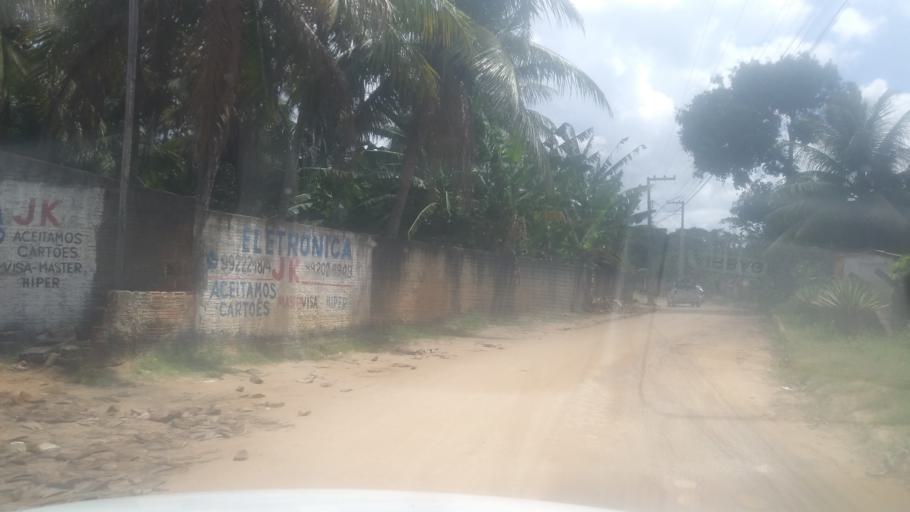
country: BR
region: Rio Grande do Norte
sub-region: Sao Jose De Mipibu
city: Sao Jose de Mipibu
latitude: -6.0717
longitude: -35.2288
